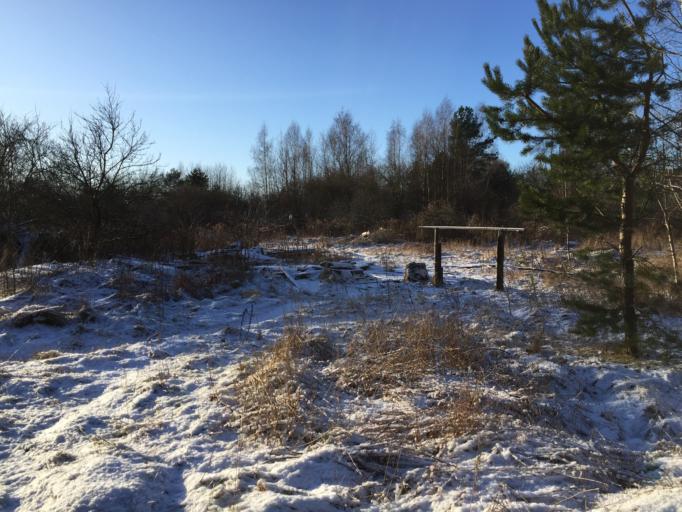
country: LV
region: Kekava
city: Balozi
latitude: 56.9102
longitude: 24.1364
